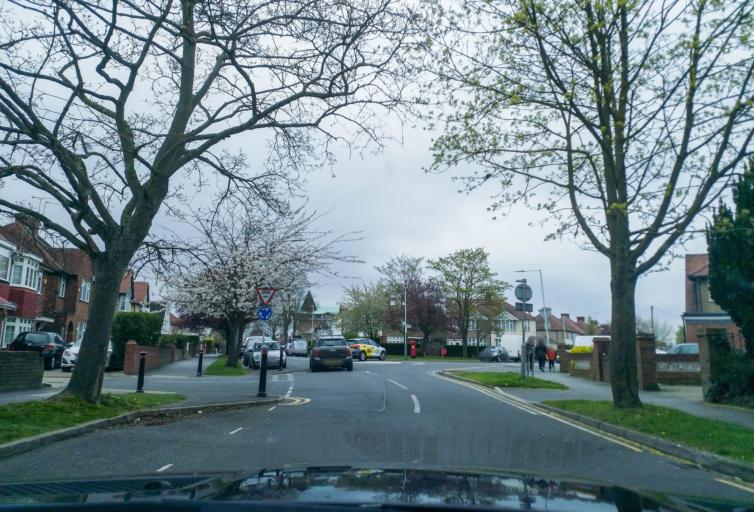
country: GB
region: England
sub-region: Greater London
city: Northolt
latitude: 51.5582
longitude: -0.3951
